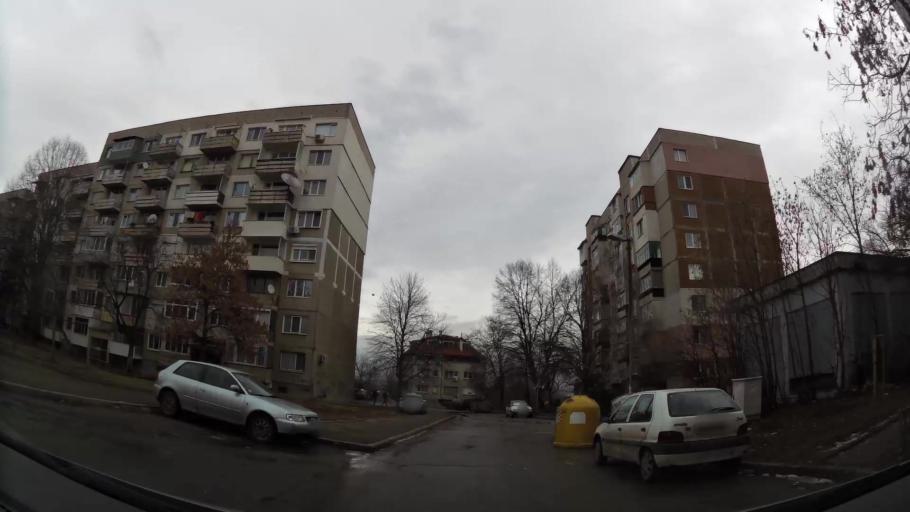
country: BG
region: Sofiya
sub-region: Obshtina Bozhurishte
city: Bozhurishte
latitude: 42.7260
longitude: 23.2571
